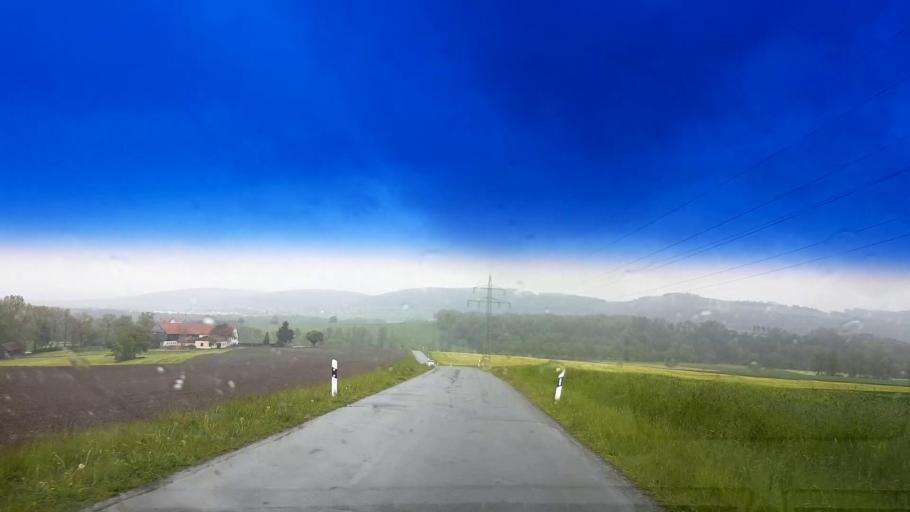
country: DE
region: Bavaria
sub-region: Upper Franconia
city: Gesees
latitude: 50.0261
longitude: 11.6271
